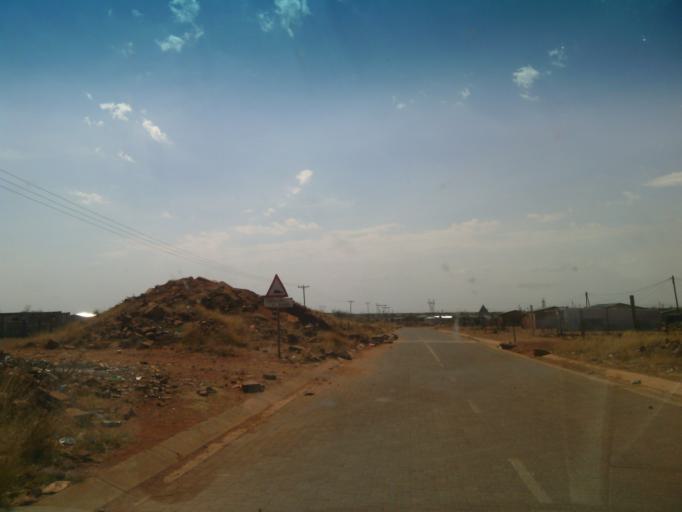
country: ZA
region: Northern Cape
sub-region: Frances Baard District Municipality
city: Barkly West
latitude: -28.5230
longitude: 24.4986
